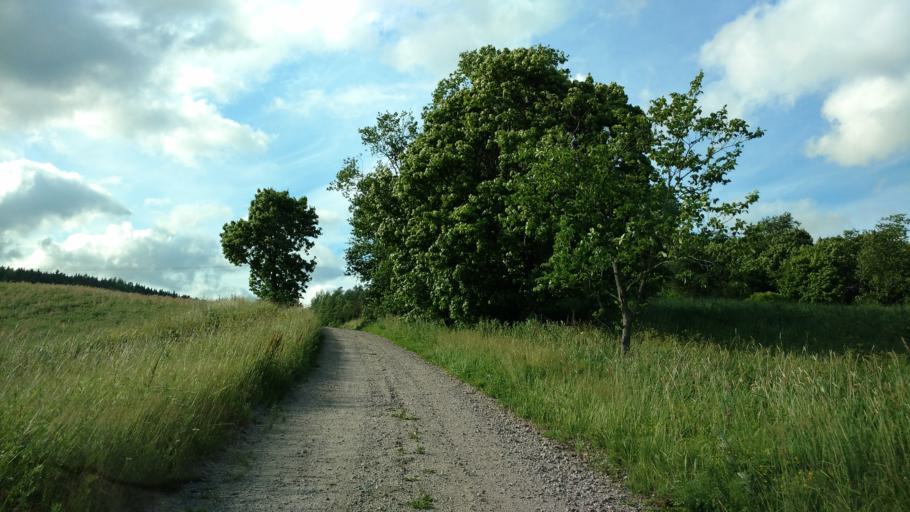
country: FI
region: Varsinais-Suomi
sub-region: Salo
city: Salo
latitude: 60.4243
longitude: 23.1765
